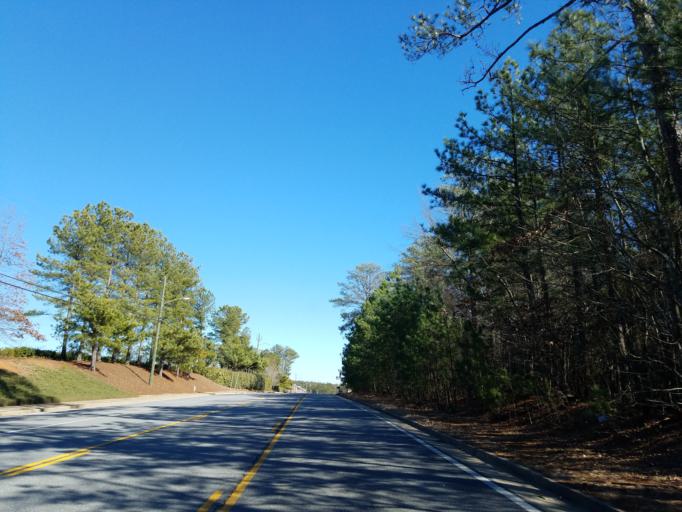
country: US
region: Georgia
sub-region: Fulton County
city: Alpharetta
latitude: 34.0500
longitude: -84.3232
